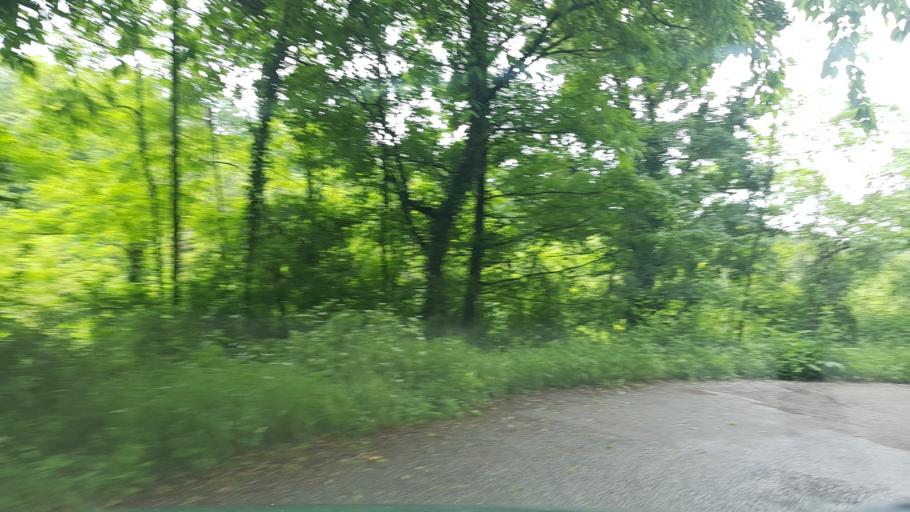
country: IT
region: Friuli Venezia Giulia
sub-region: Provincia di Gorizia
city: San Floriano del Collio
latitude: 45.9496
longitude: 13.5849
